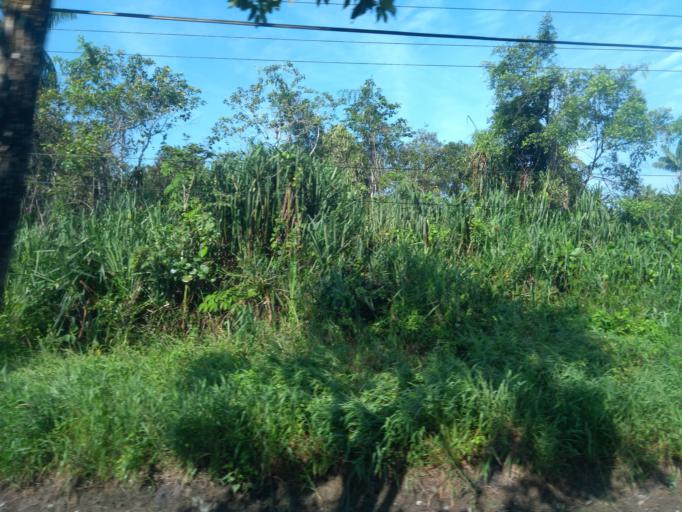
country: MY
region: Sarawak
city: Kuching
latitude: 1.6533
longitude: 110.4441
